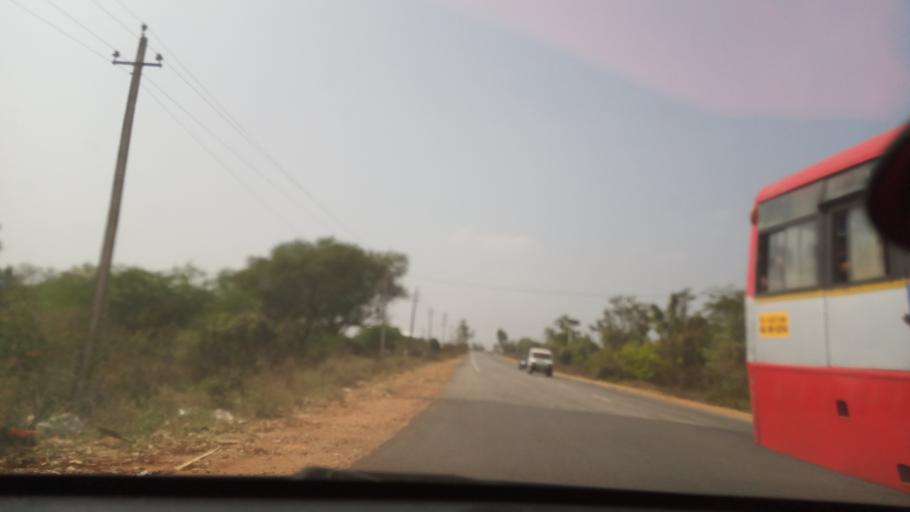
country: IN
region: Karnataka
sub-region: Mysore
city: Nanjangud
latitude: 12.0907
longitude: 76.7253
